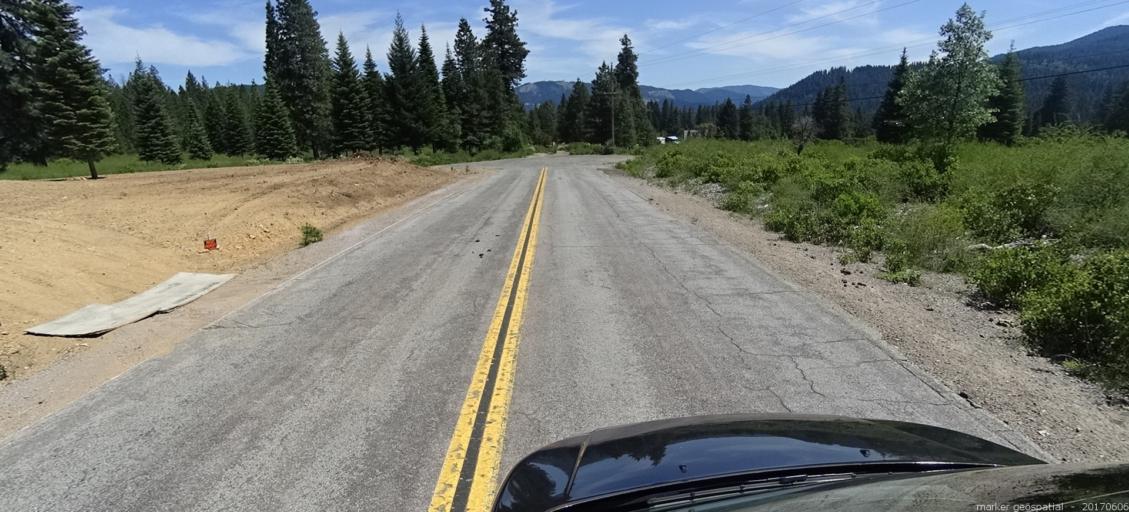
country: US
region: California
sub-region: Siskiyou County
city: Mount Shasta
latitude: 41.2798
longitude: -122.2912
